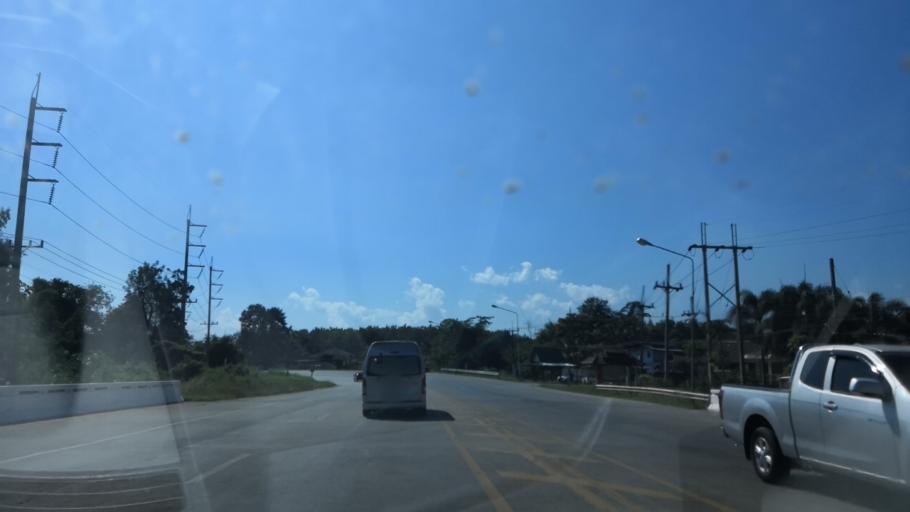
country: TH
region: Chiang Rai
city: Mae Suai
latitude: 19.6362
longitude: 99.5170
